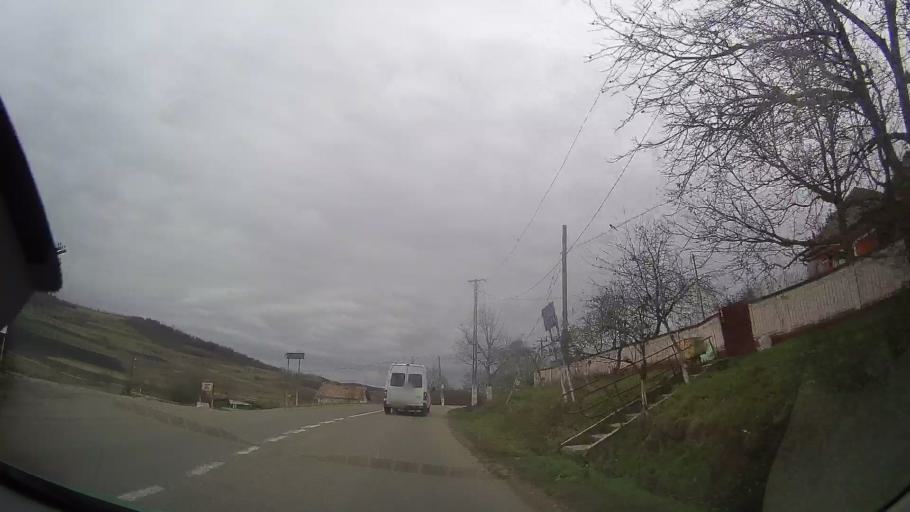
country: RO
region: Cluj
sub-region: Comuna Catina
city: Catina
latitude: 46.7971
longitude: 24.2132
